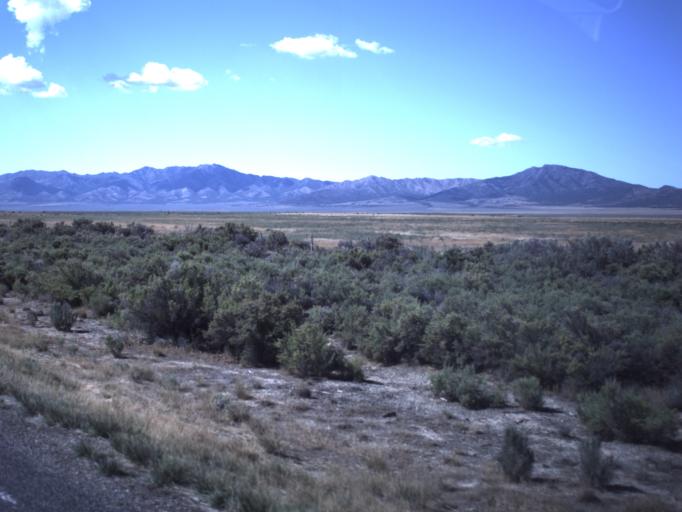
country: US
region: Utah
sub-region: Tooele County
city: Tooele
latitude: 40.1462
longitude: -112.4308
